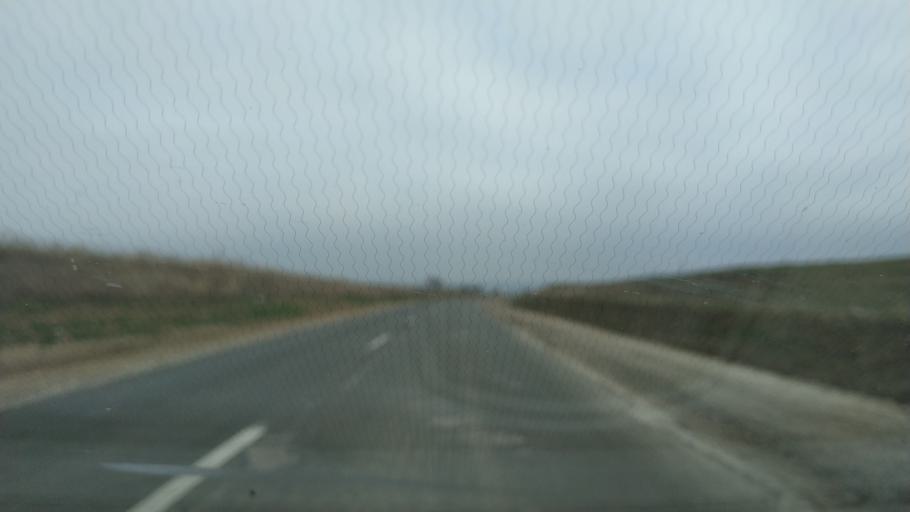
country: MD
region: Straseni
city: Taraclia
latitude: 45.9348
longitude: 28.5850
